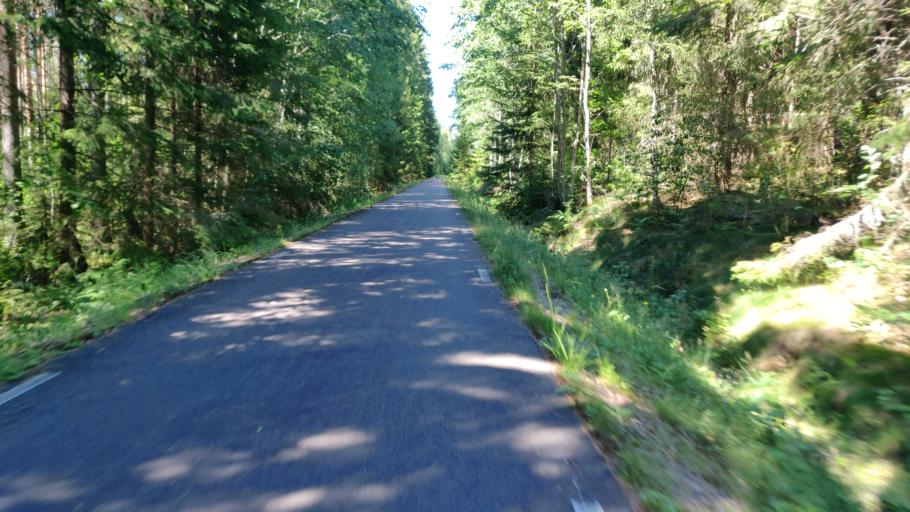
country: SE
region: Vaermland
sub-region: Hagfors Kommun
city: Hagfors
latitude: 59.9537
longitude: 13.5759
